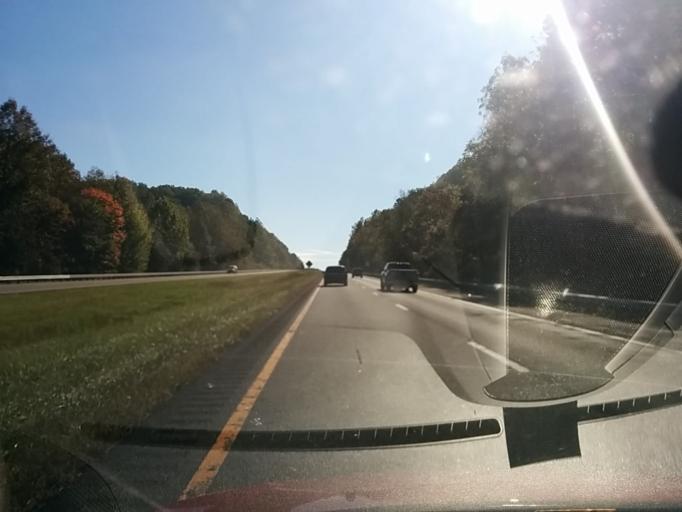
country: US
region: Virginia
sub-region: City of Charlottesville
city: Charlottesville
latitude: 38.0288
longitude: -78.5915
